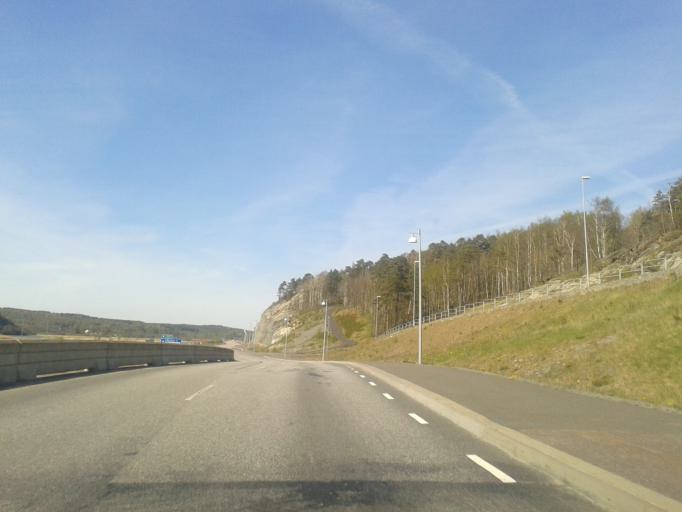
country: SE
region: Vaestra Goetaland
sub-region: Ale Kommun
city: Nodinge-Nol
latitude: 57.8772
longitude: 12.0384
